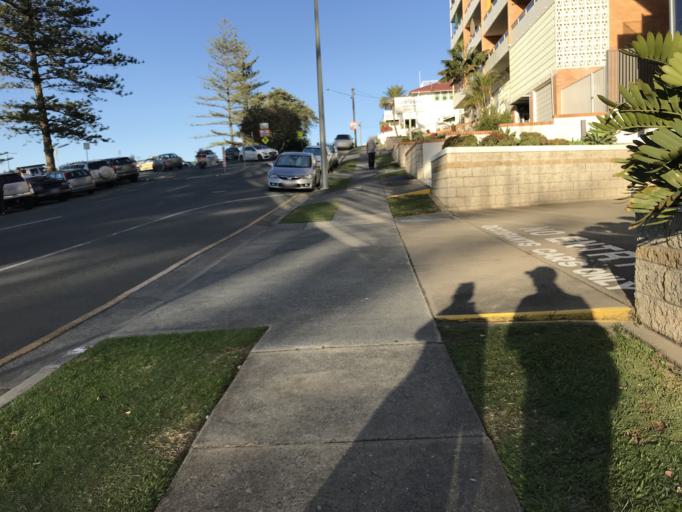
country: AU
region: Queensland
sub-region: Gold Coast
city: Palm Beach
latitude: -28.0903
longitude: 153.4566
